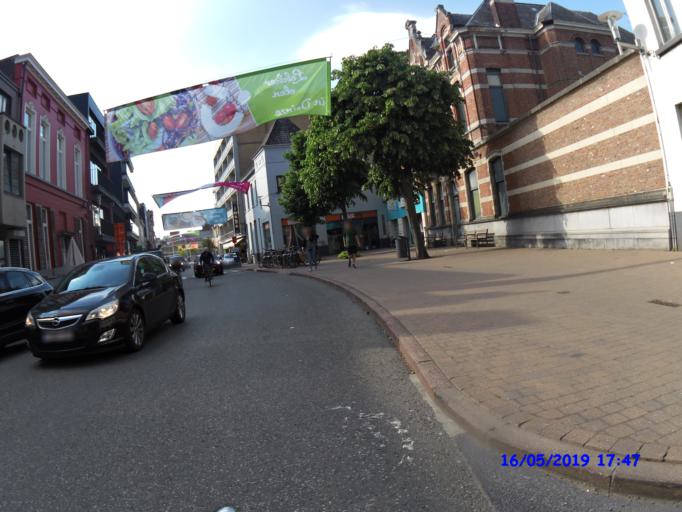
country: BE
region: Flanders
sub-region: Provincie Oost-Vlaanderen
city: Deinze
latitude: 50.9815
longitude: 3.5294
